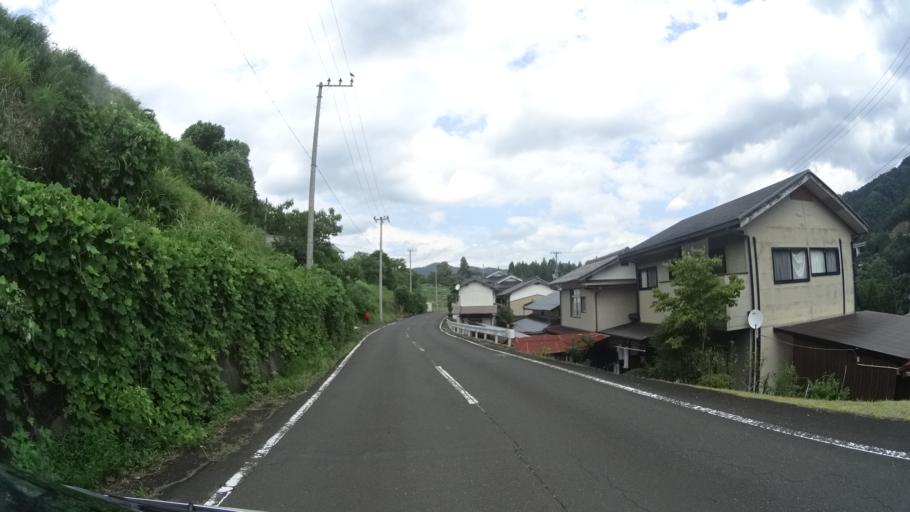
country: JP
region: Kyoto
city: Ayabe
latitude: 35.2829
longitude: 135.3318
